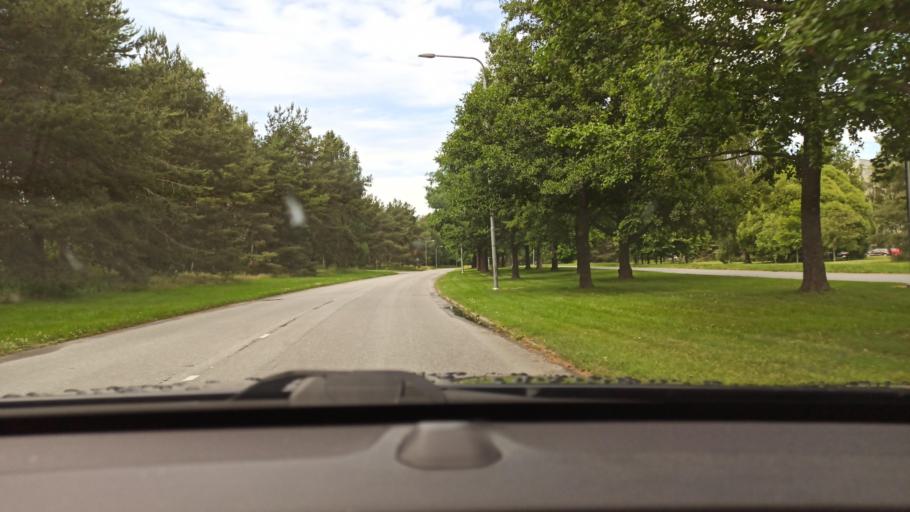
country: FI
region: Satakunta
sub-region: Pori
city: Pori
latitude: 61.5060
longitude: 21.7775
